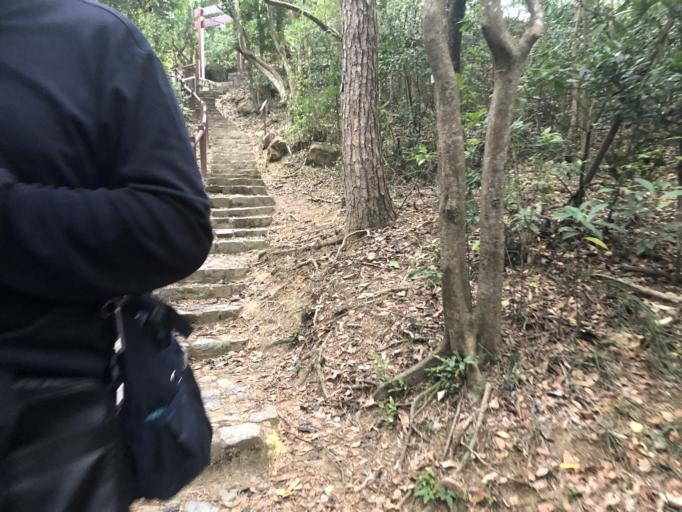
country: HK
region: Wanchai
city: Wan Chai
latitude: 22.2787
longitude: 114.2102
